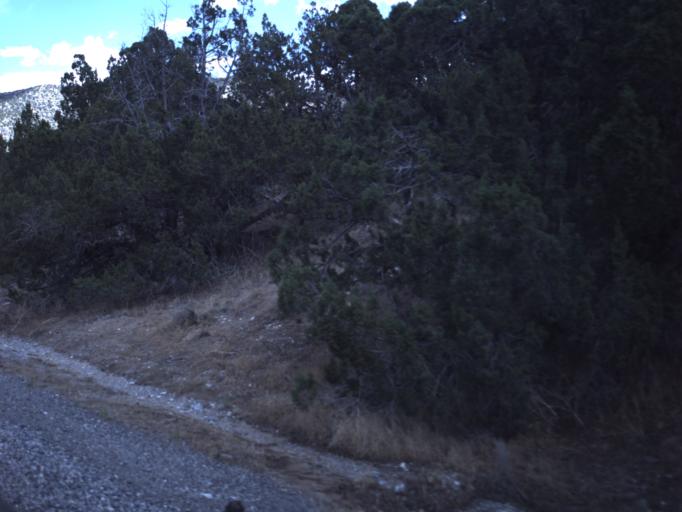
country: US
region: Utah
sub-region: Tooele County
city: Grantsville
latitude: 40.3264
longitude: -112.6234
